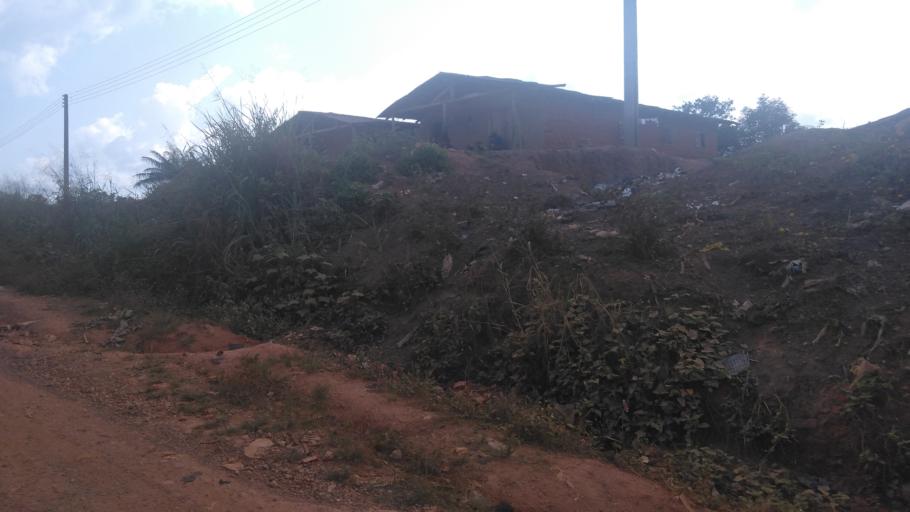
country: NG
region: Osun
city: Ifetedo
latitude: 7.0137
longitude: 4.6345
